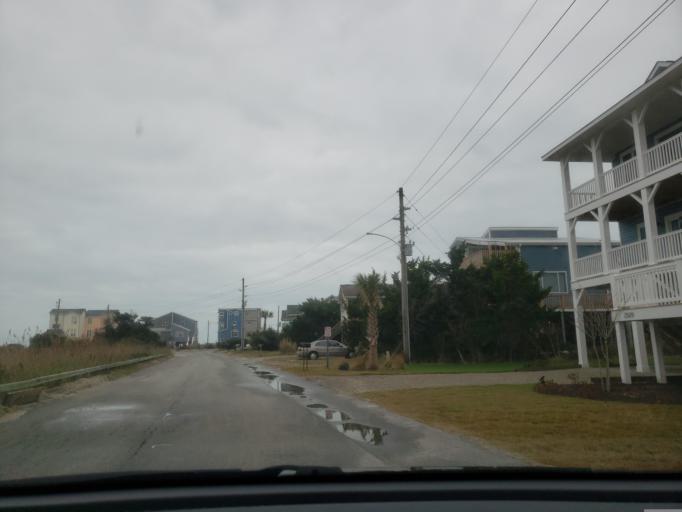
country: US
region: North Carolina
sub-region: Onslow County
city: Sneads Ferry
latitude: 34.5267
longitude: -77.3464
